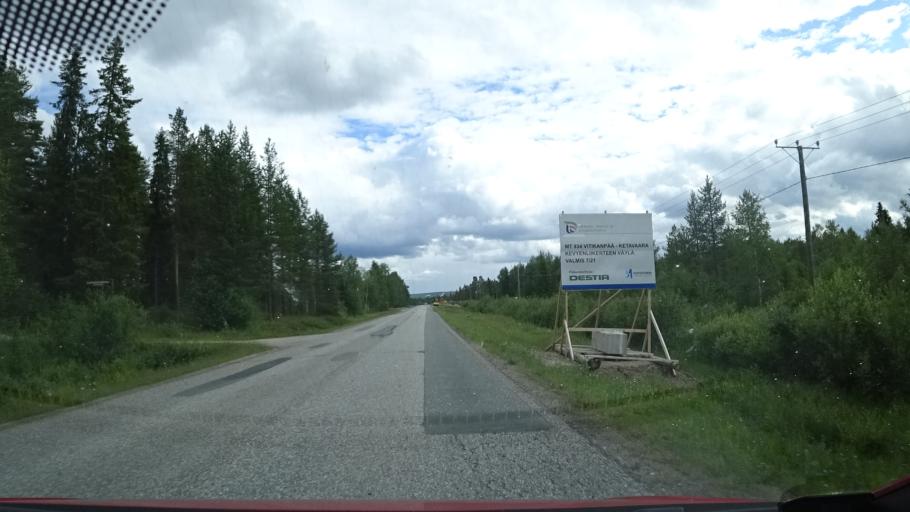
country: FI
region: Lapland
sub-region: Rovaniemi
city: Rovaniemi
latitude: 66.5446
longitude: 25.7090
